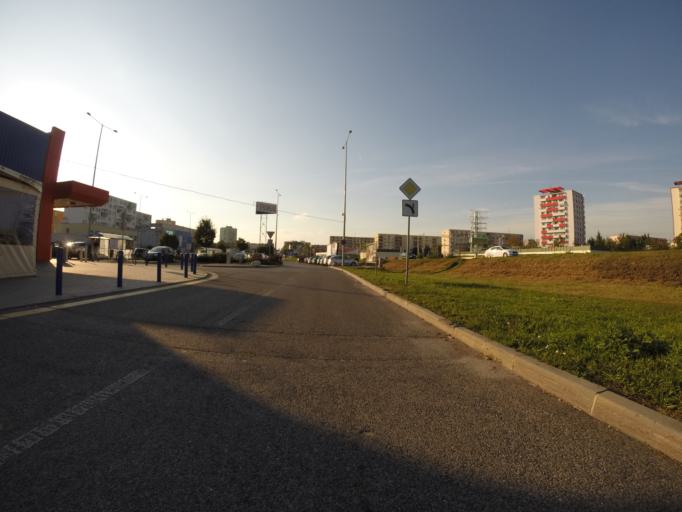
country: SK
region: Nitriansky
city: Banovce nad Bebravou
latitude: 48.5550
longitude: 18.1813
